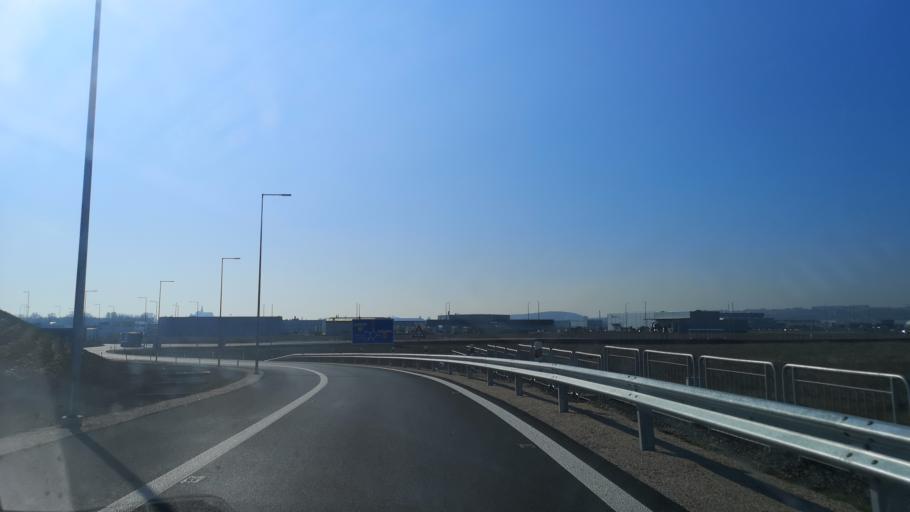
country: SK
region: Nitriansky
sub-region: Okres Nitra
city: Nitra
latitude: 48.3421
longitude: 18.0576
